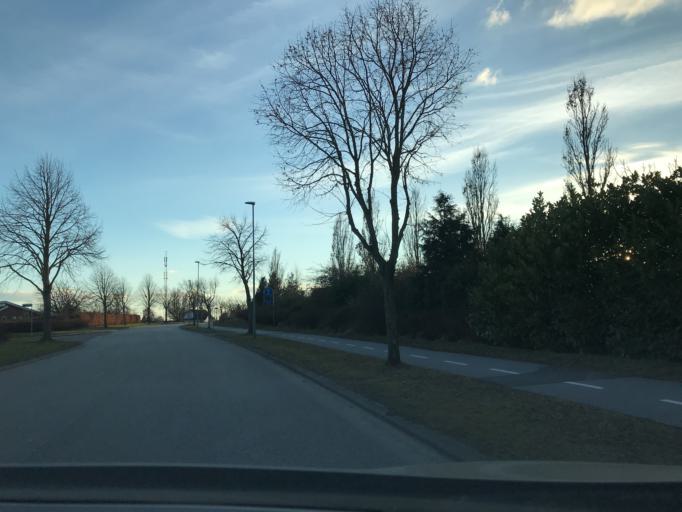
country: DK
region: South Denmark
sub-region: Middelfart Kommune
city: Norre Aby
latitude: 55.4615
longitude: 9.8870
